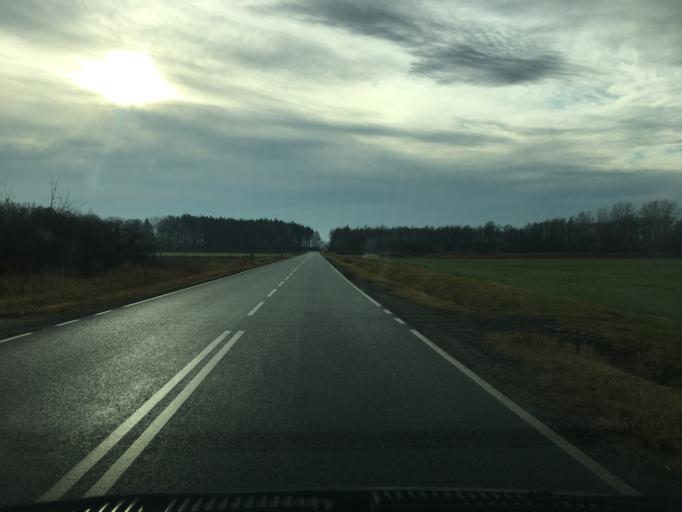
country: PL
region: Lower Silesian Voivodeship
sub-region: Powiat wroclawski
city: Dlugoleka
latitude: 51.1814
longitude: 17.2231
